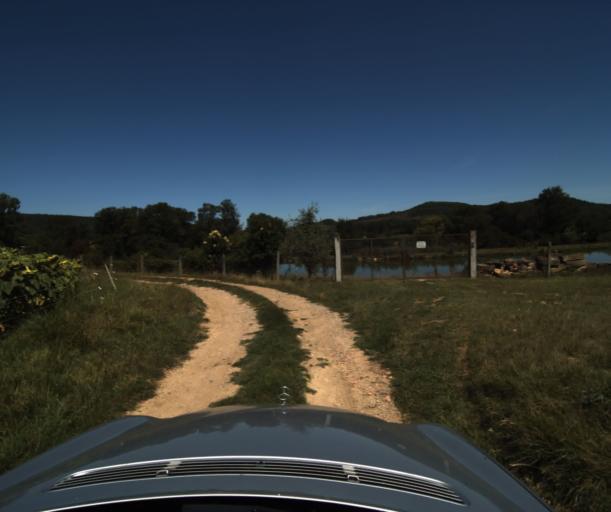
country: FR
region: Languedoc-Roussillon
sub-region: Departement de l'Aude
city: Chalabre
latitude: 42.9903
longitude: 1.9191
